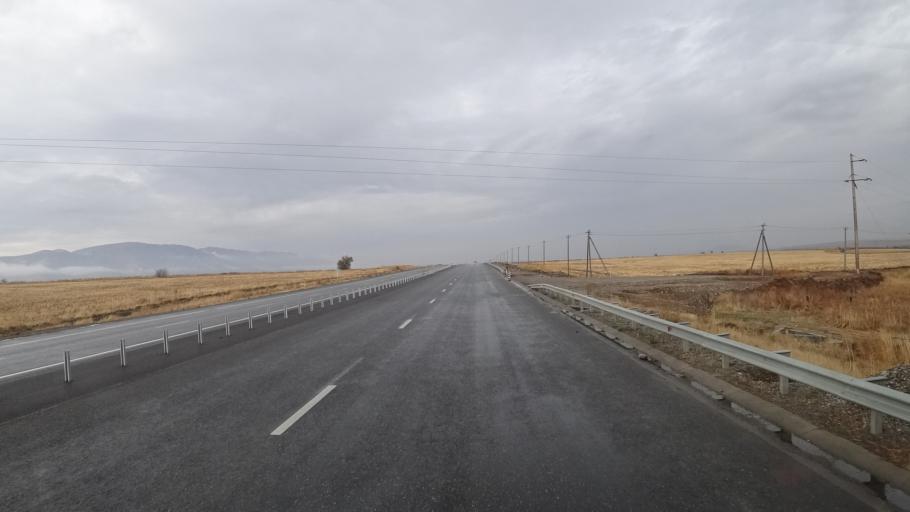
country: KZ
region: Ongtustik Qazaqstan
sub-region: Tulkibas Audany
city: Zhabagly
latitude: 42.5070
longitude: 70.4411
